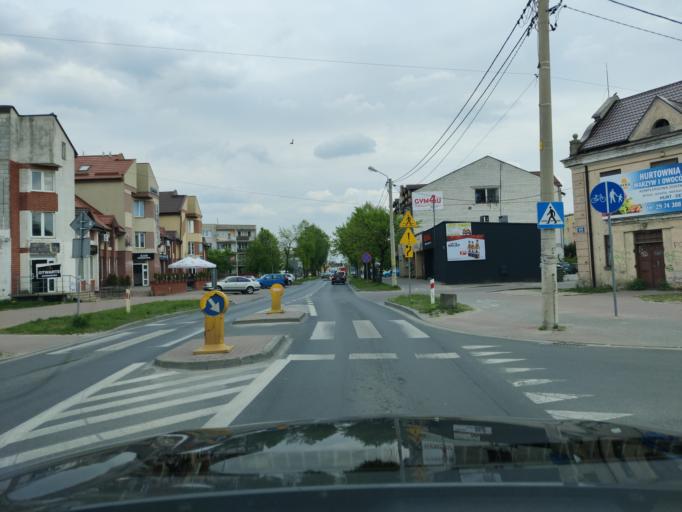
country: PL
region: Masovian Voivodeship
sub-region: Powiat wyszkowski
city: Wyszkow
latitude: 52.5977
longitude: 21.4457
